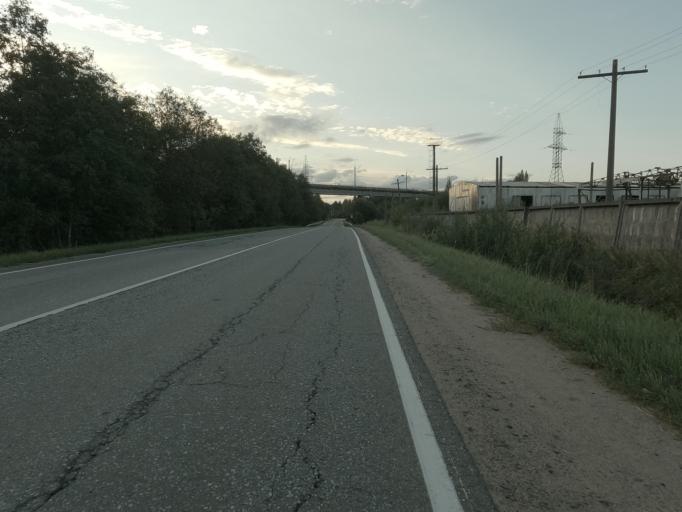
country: RU
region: Leningrad
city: Mga
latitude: 59.7573
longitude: 31.0201
